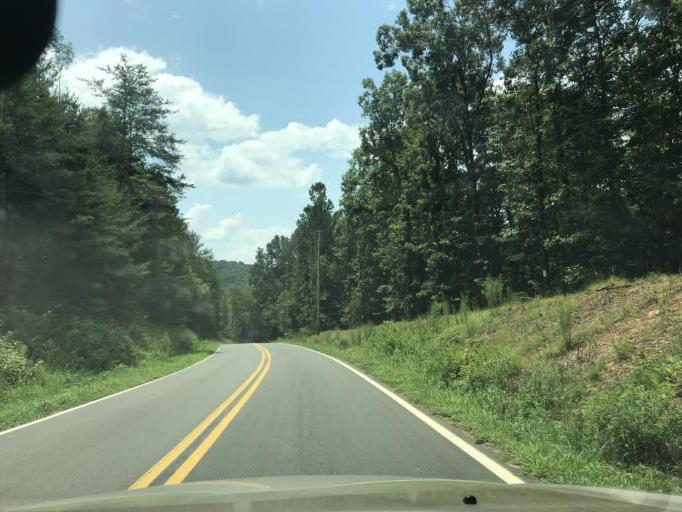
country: US
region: Georgia
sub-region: Forsyth County
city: Cumming
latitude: 34.3158
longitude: -84.2209
